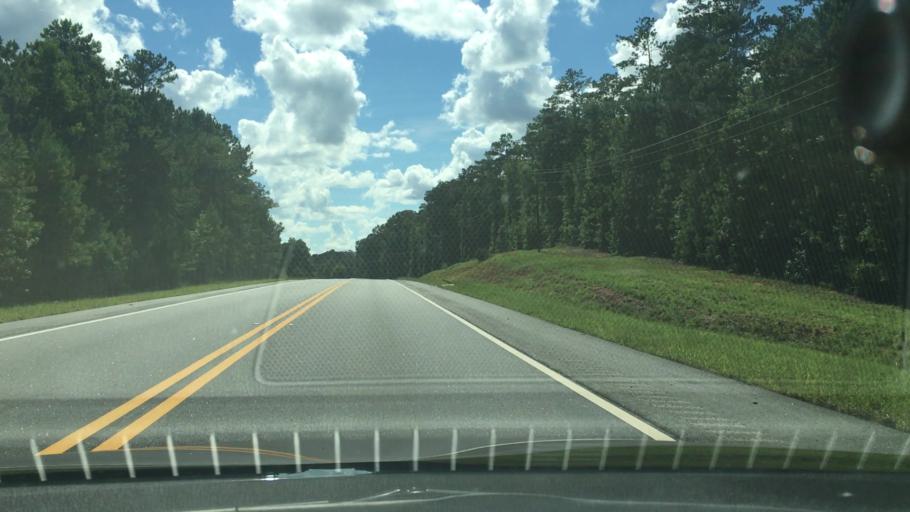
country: US
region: Georgia
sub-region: Butts County
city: Indian Springs
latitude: 33.3046
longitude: -83.8432
